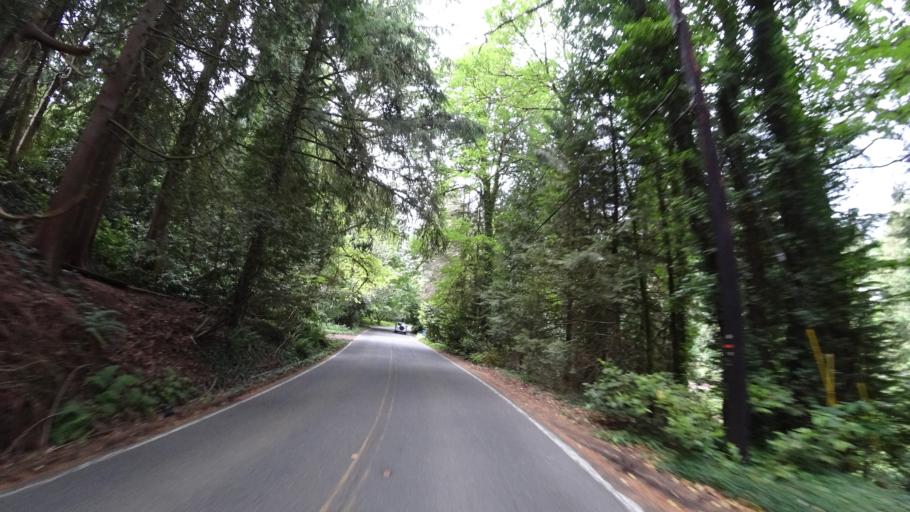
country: US
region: Oregon
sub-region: Clackamas County
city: Lake Oswego
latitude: 45.4568
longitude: -122.7009
